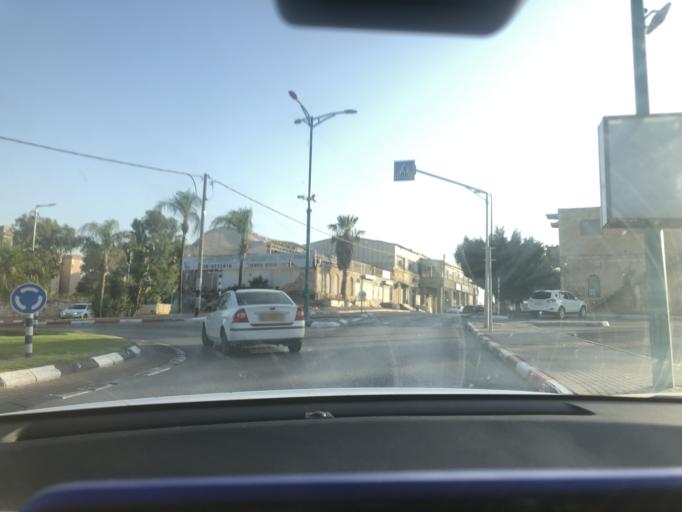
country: IL
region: Central District
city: Lod
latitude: 31.9501
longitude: 34.8954
